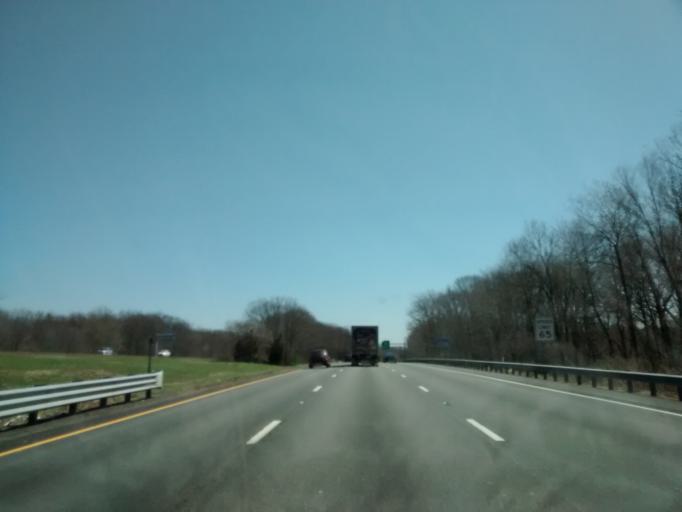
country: US
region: Massachusetts
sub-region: Worcester County
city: Milford
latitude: 42.1627
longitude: -71.5001
